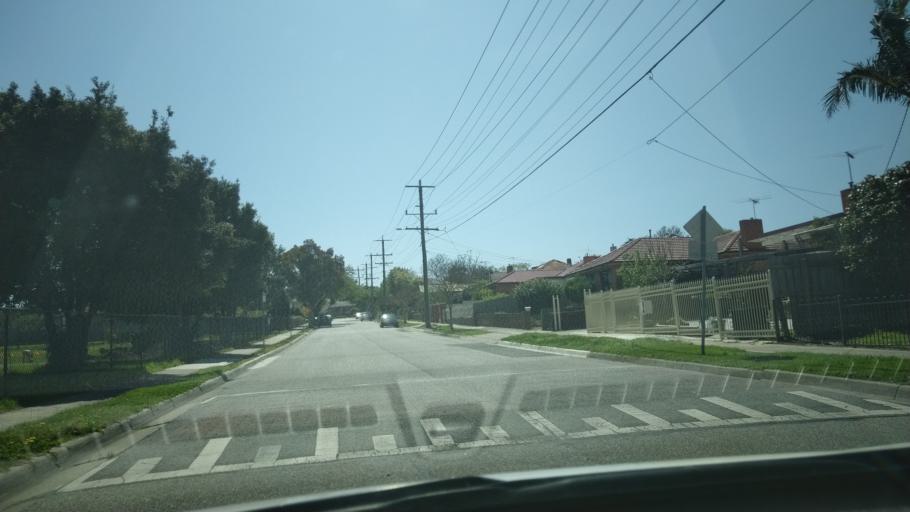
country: AU
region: Victoria
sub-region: Greater Dandenong
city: Noble Park
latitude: -37.9690
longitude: 145.1608
